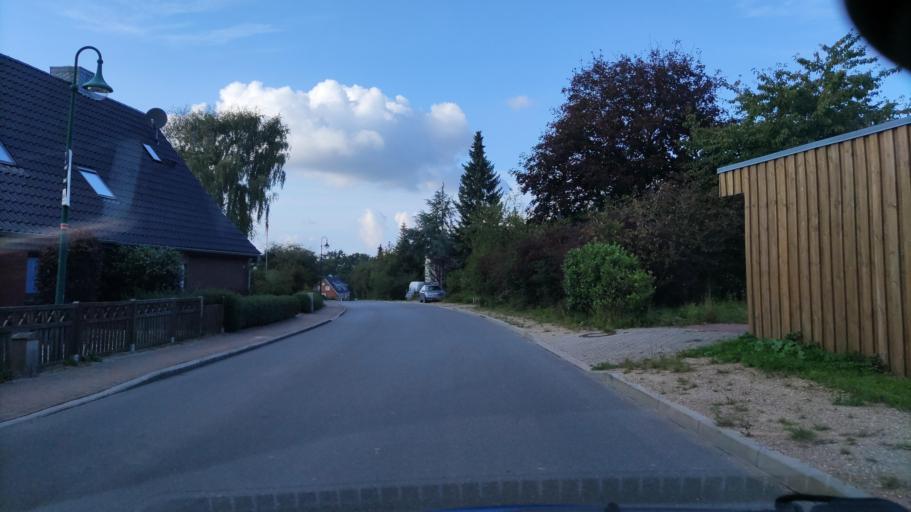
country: DE
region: Schleswig-Holstein
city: Glasau
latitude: 54.0499
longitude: 10.5305
